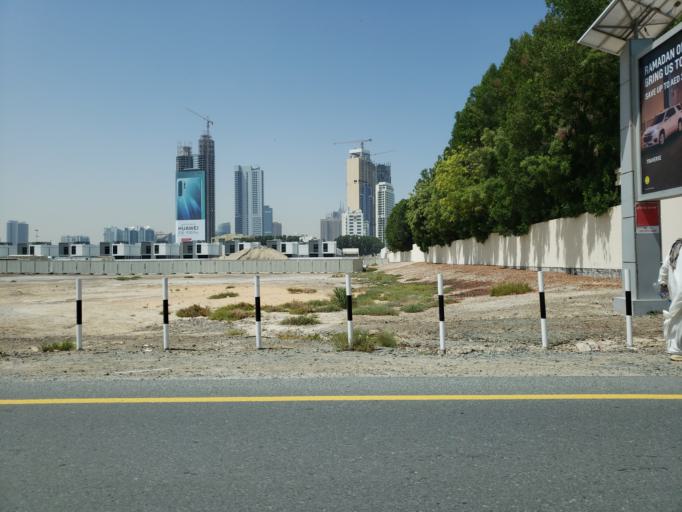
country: AE
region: Dubai
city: Dubai
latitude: 25.1163
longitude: 55.1837
